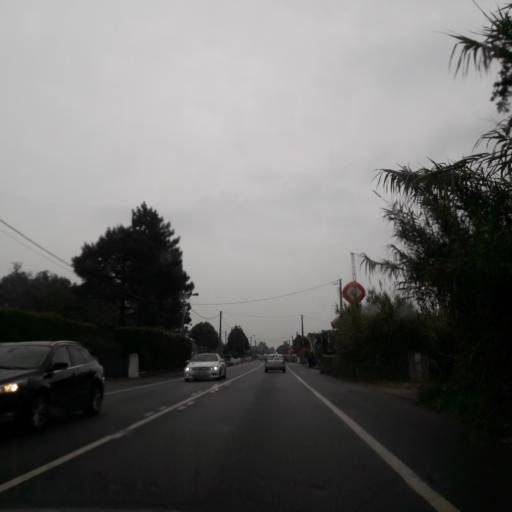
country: PT
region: Porto
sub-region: Vila do Conde
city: Arvore
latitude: 41.3138
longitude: -8.7081
